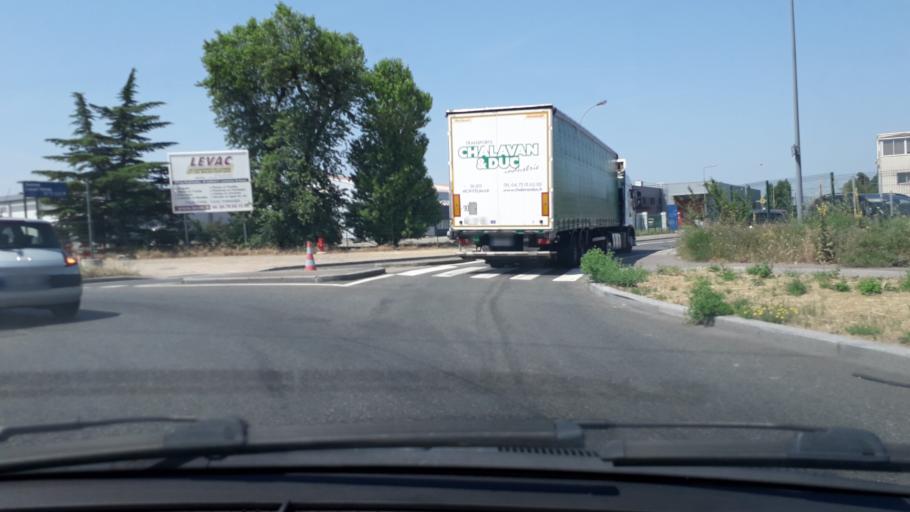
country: FR
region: Rhone-Alpes
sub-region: Departement du Rhone
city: Jonage
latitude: 45.7702
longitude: 5.0316
